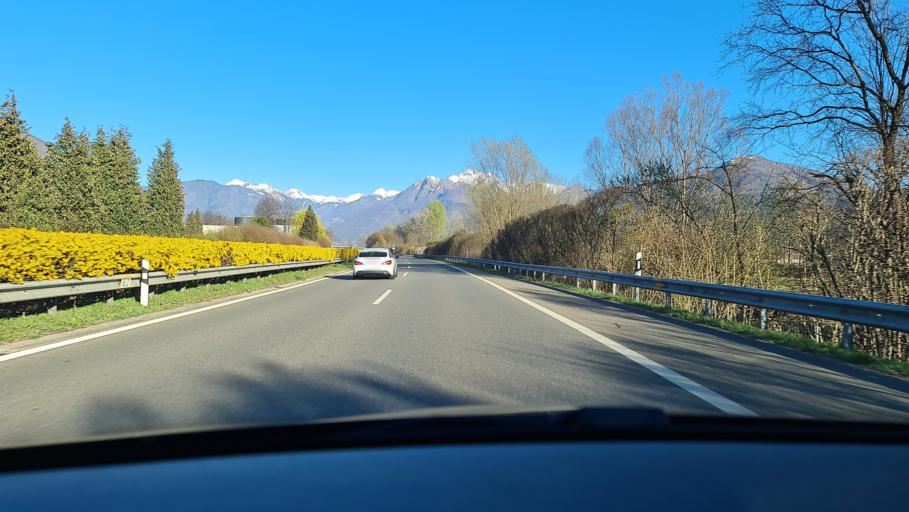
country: CH
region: Ticino
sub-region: Locarno District
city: Gordola
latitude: 46.1682
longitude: 8.8693
